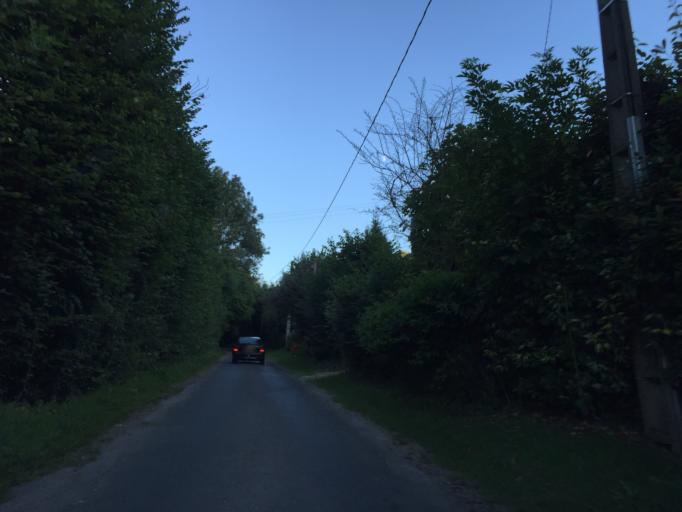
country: FR
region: Lower Normandy
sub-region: Departement du Calvados
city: Equemauville
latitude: 49.4103
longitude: 0.2028
